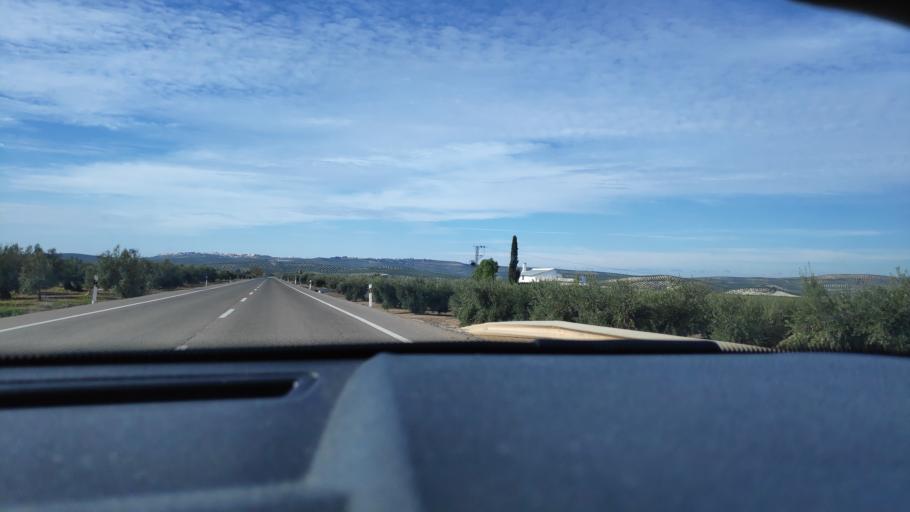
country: ES
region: Andalusia
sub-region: Provincia de Jaen
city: Higuera de Calatrava
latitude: 37.8421
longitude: -4.1120
